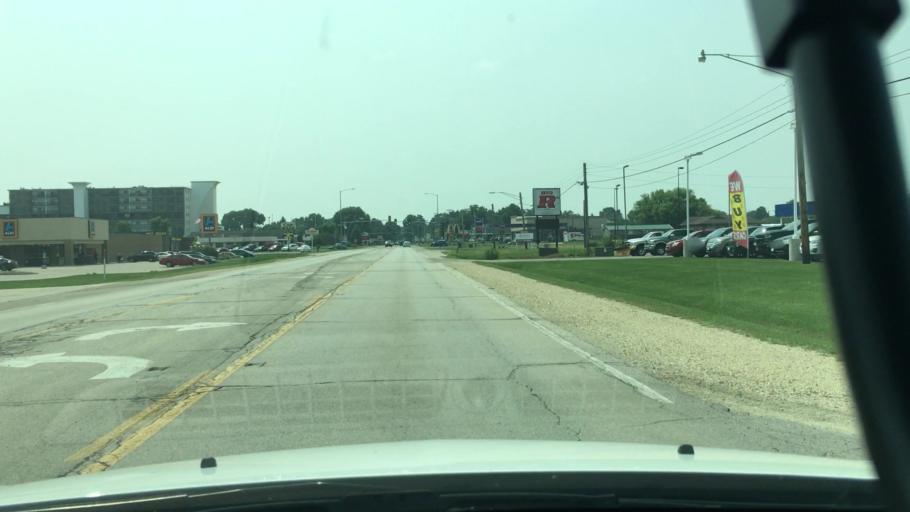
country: US
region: Illinois
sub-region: Ogle County
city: Hillcrest
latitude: 41.9382
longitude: -89.0682
